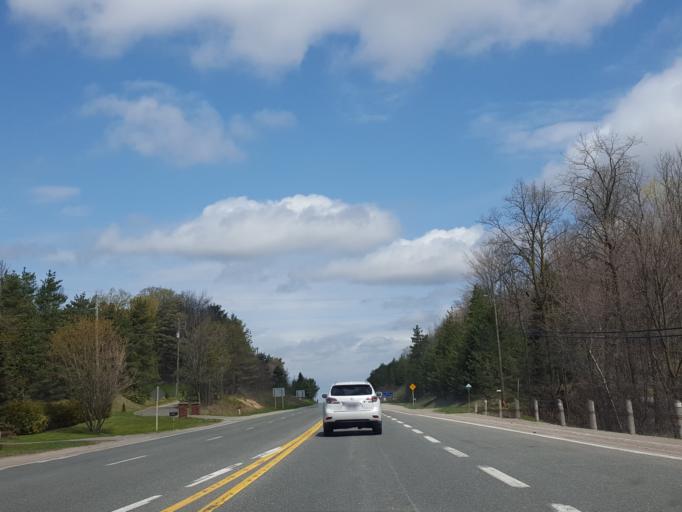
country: CA
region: Ontario
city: Newmarket
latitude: 44.0952
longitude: -79.3104
